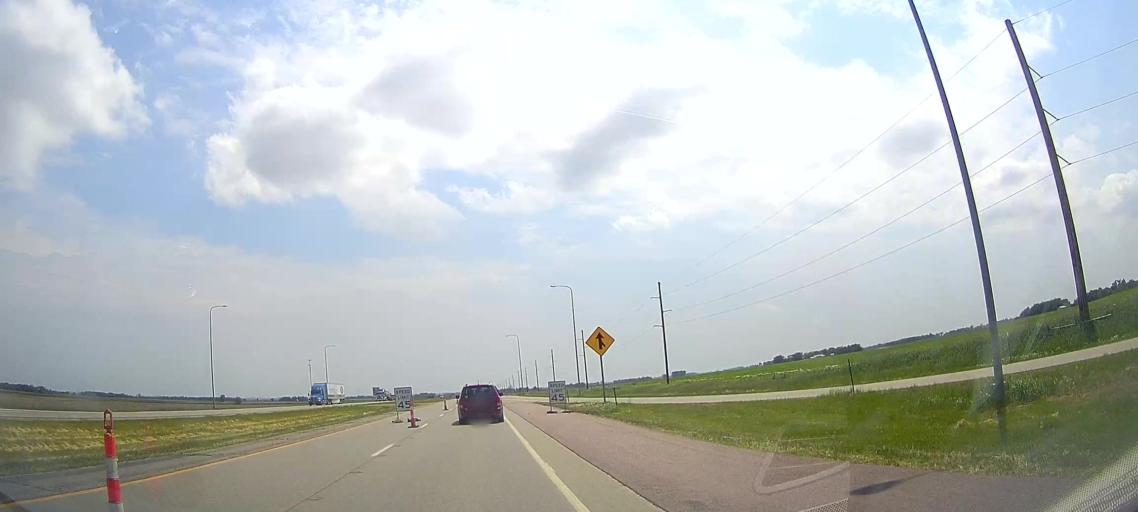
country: US
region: South Dakota
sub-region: Lincoln County
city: Lennox
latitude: 43.2981
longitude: -96.7964
